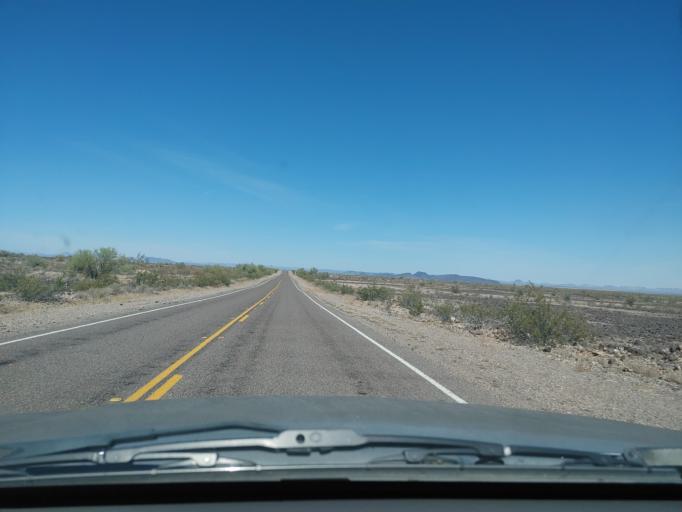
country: US
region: Arizona
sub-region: Maricopa County
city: Gila Bend
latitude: 32.8972
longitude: -113.2510
